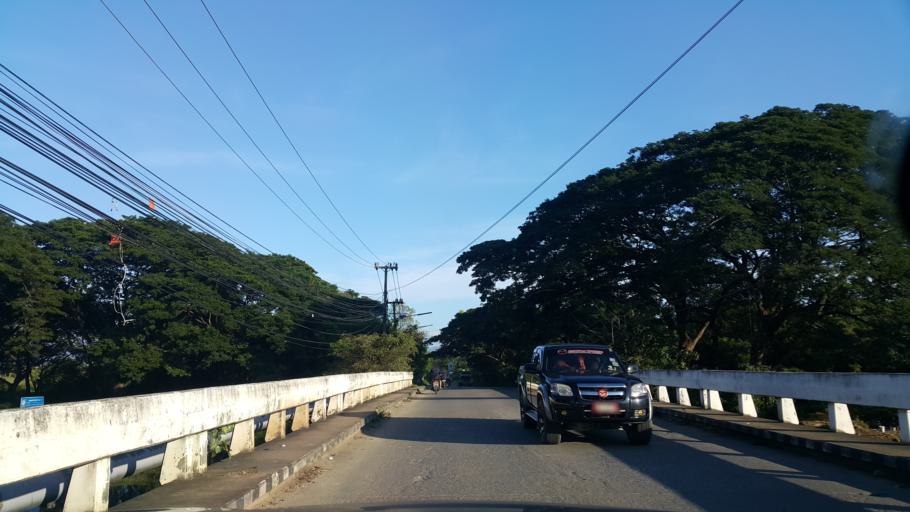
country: TH
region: Lamphun
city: Lamphun
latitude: 18.5976
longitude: 99.0305
